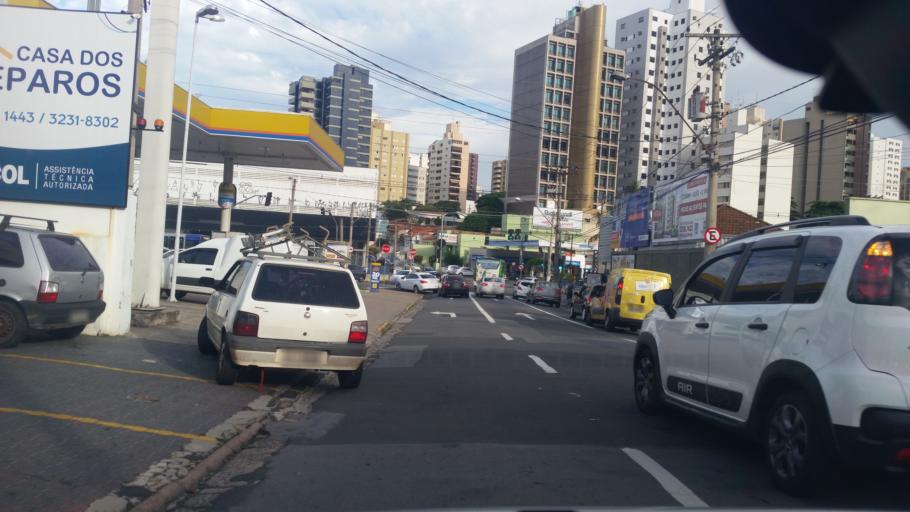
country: BR
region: Sao Paulo
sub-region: Campinas
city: Campinas
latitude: -22.8892
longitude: -47.0583
